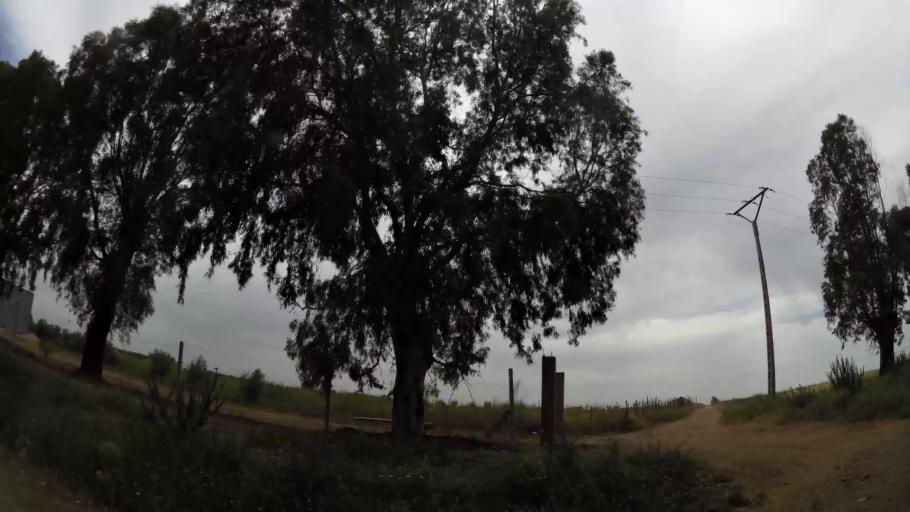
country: MA
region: Rabat-Sale-Zemmour-Zaer
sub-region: Khemisset
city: Tiflet
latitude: 33.8642
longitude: -6.2727
